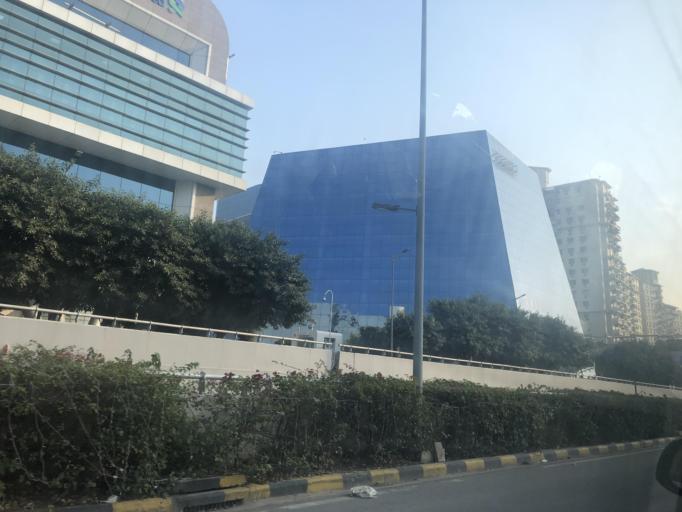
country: IN
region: Haryana
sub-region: Gurgaon
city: Gurgaon
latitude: 28.4925
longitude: 77.0915
